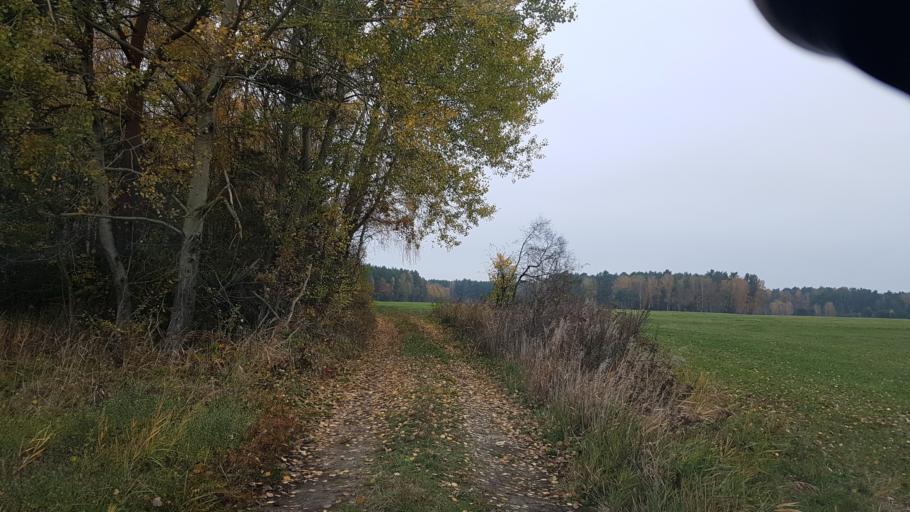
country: DE
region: Brandenburg
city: Ruckersdorf
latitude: 51.5715
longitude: 13.6453
